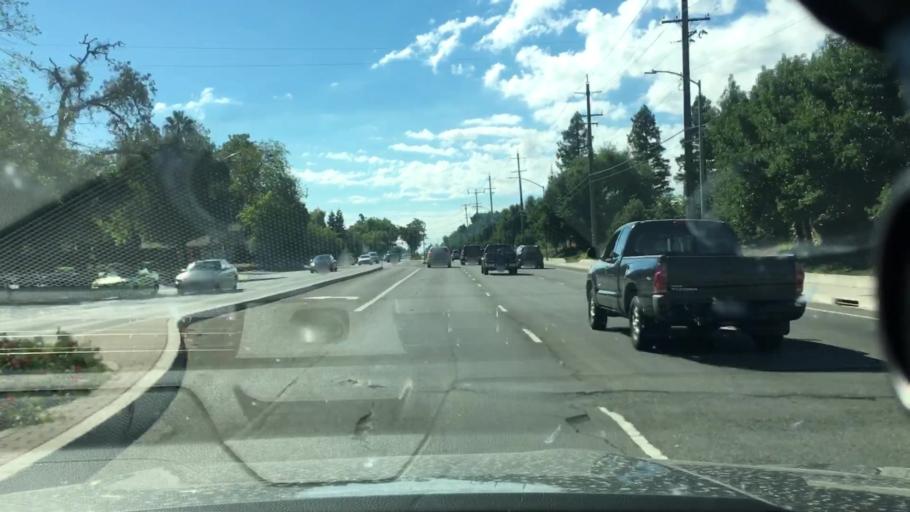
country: US
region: California
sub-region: Sacramento County
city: Arden-Arcade
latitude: 38.6222
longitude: -121.3830
